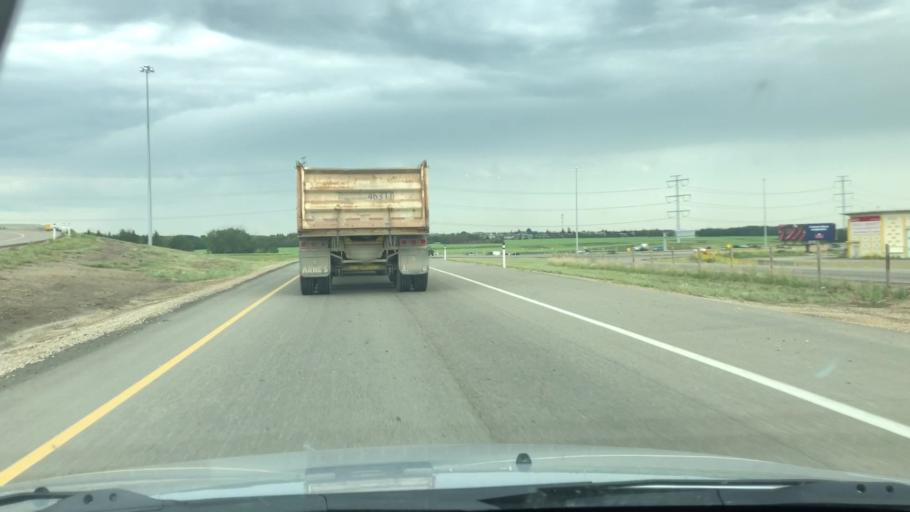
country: CA
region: Alberta
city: Sherwood Park
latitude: 53.5112
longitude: -113.3474
